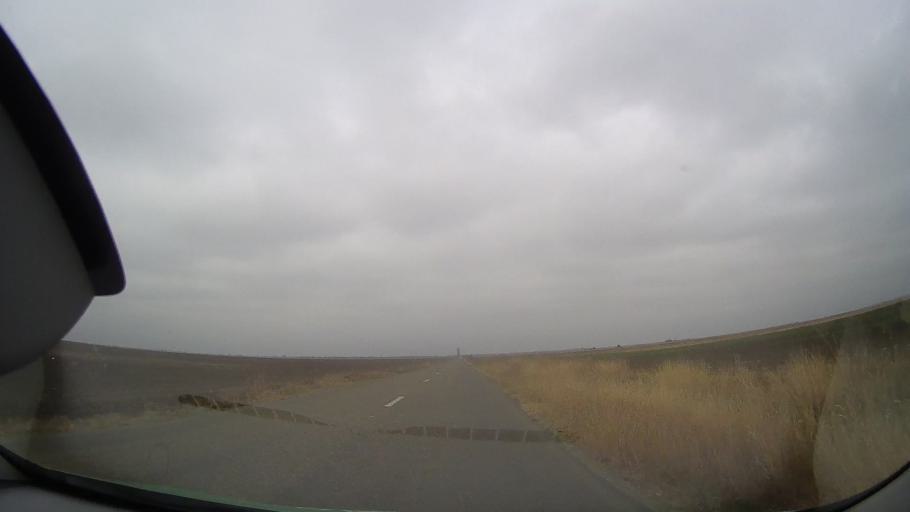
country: RO
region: Buzau
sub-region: Comuna Bradeanu
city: Bradeanu
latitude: 44.8956
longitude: 26.8732
